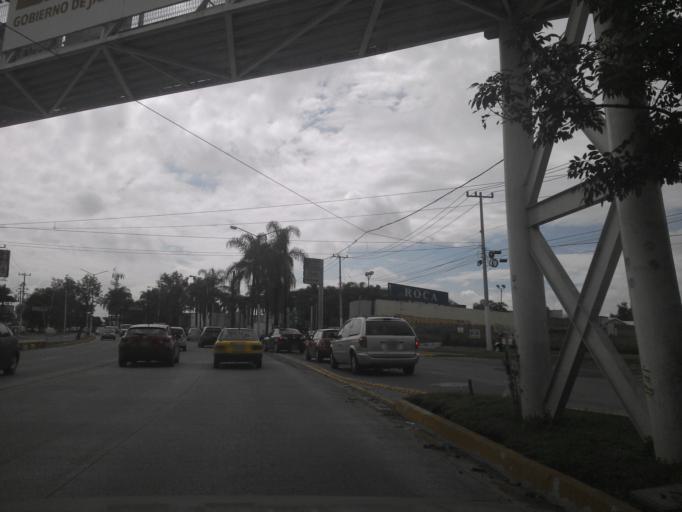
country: MX
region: Jalisco
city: Guadalajara
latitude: 20.6832
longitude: -103.4398
